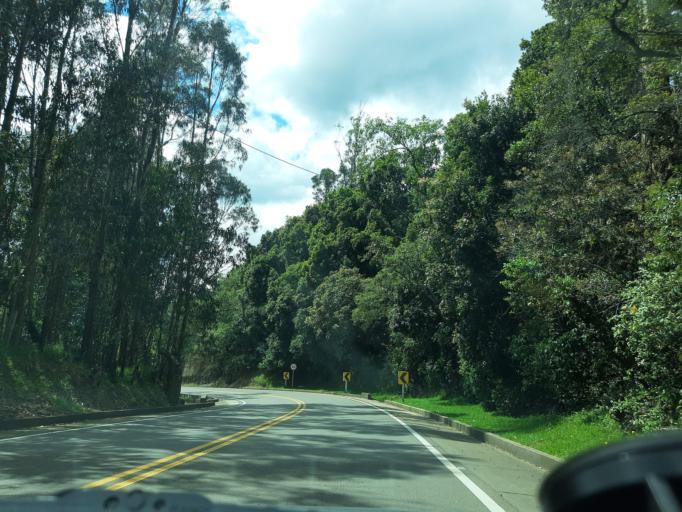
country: CO
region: Boyaca
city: Raquira
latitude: 5.5882
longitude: -73.7012
